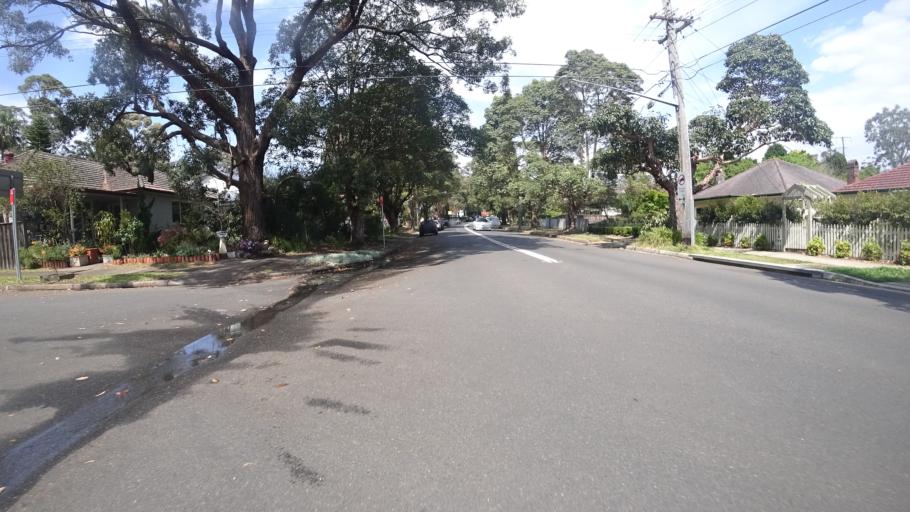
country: AU
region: New South Wales
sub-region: Hornsby Shire
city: Mount Colah
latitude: -33.6864
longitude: 151.1108
